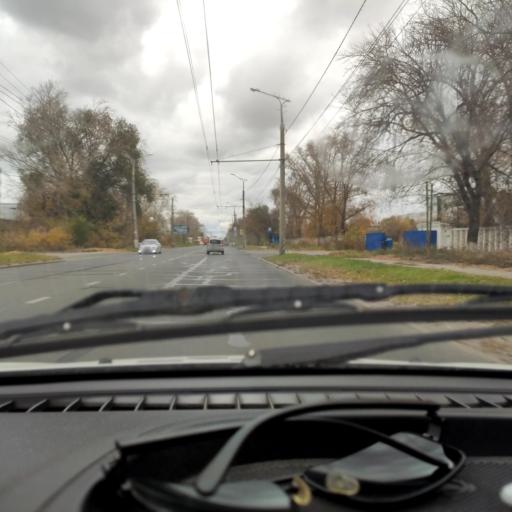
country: RU
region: Samara
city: Tol'yatti
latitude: 53.5271
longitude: 49.4361
